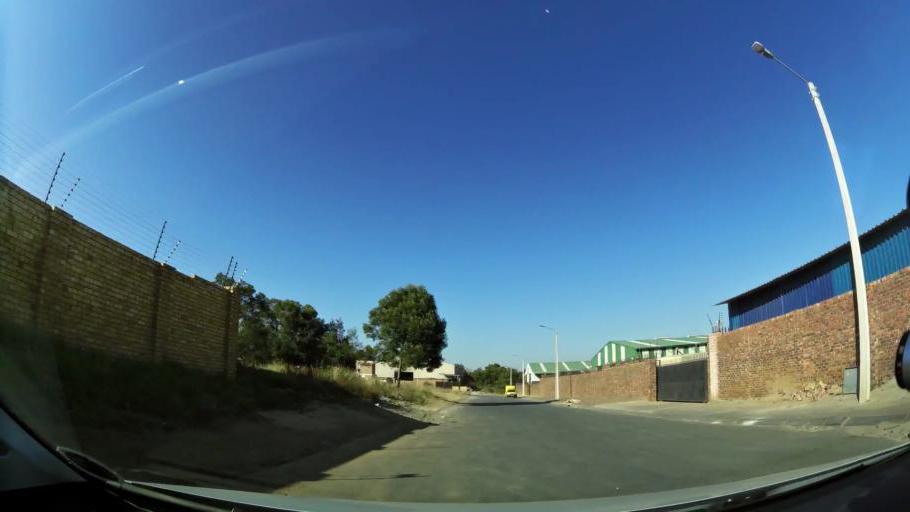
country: ZA
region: Gauteng
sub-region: City of Johannesburg Metropolitan Municipality
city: Modderfontein
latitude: -26.0621
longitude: 28.1758
